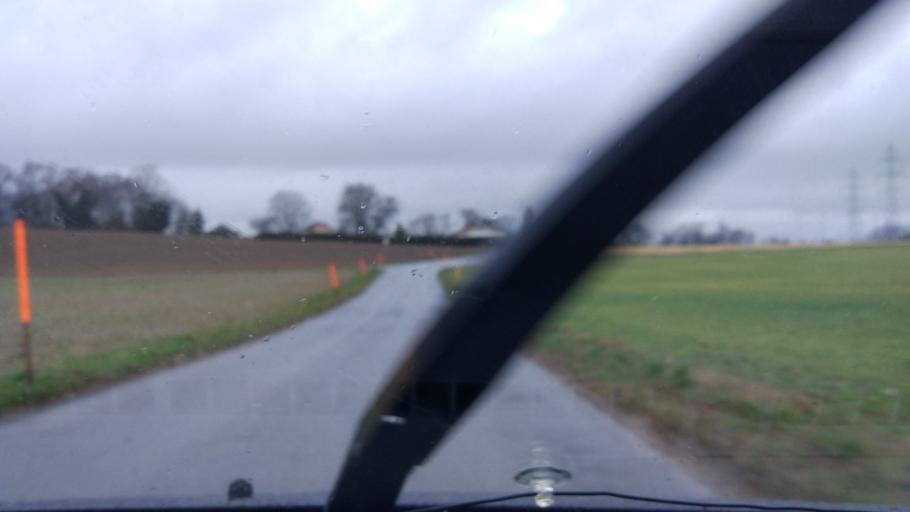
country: CH
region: Vaud
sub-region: Lausanne District
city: Romanel
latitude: 46.5558
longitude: 6.6046
